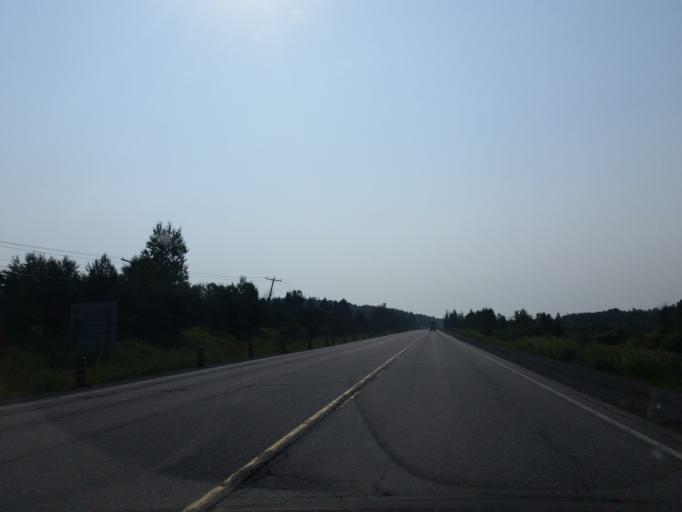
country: CA
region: Ontario
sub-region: Nipissing District
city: North Bay
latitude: 46.4256
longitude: -80.1914
